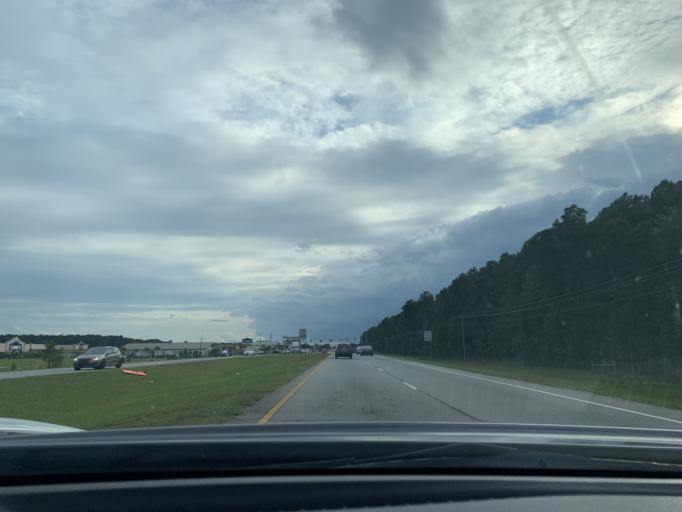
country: US
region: Georgia
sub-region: Chatham County
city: Pooler
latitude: 32.0957
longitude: -81.2731
